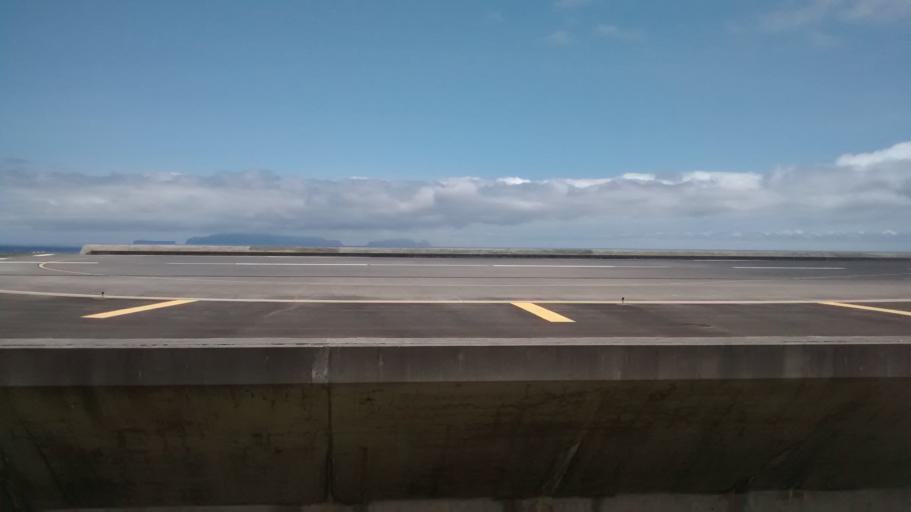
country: PT
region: Madeira
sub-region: Machico
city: Machico
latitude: 32.7073
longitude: -16.7651
